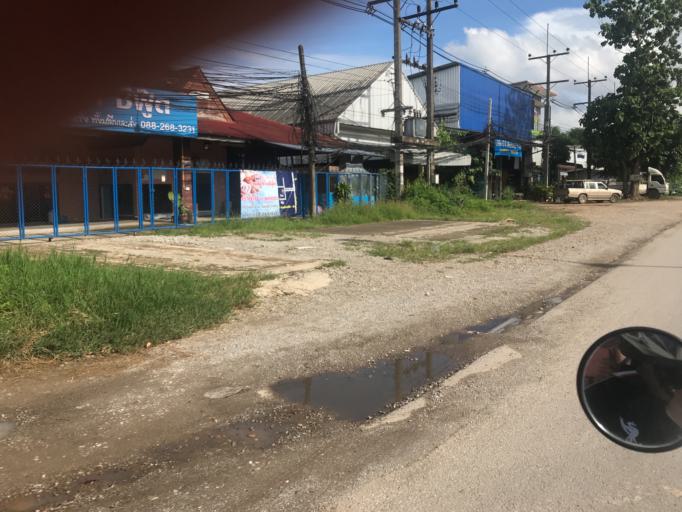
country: TH
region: Chiang Rai
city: Chiang Rai
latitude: 19.9424
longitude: 99.8463
